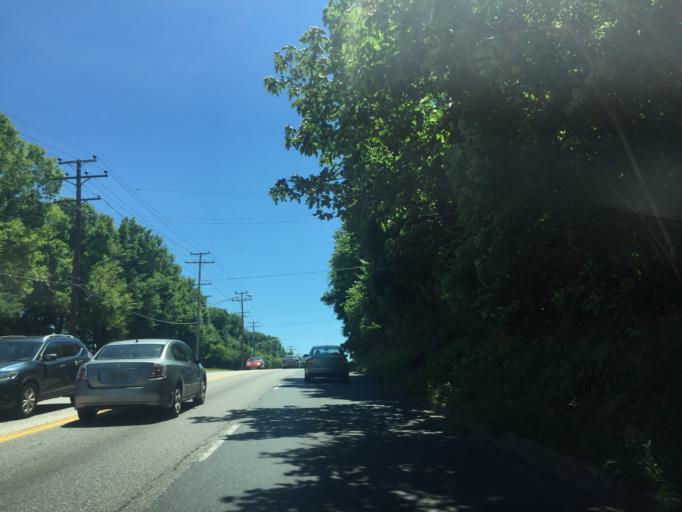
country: US
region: Maryland
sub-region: Baltimore County
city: Garrison
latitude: 39.4026
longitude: -76.7558
